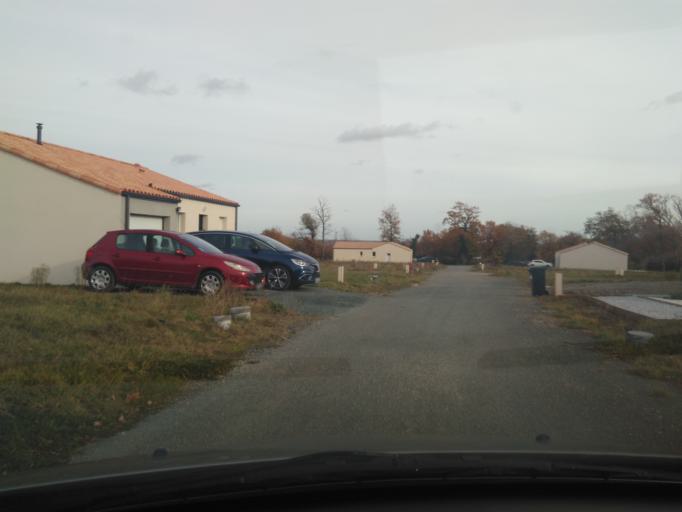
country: FR
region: Pays de la Loire
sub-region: Departement de la Vendee
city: Saint-Florent-des-Bois
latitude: 46.5872
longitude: -1.3197
